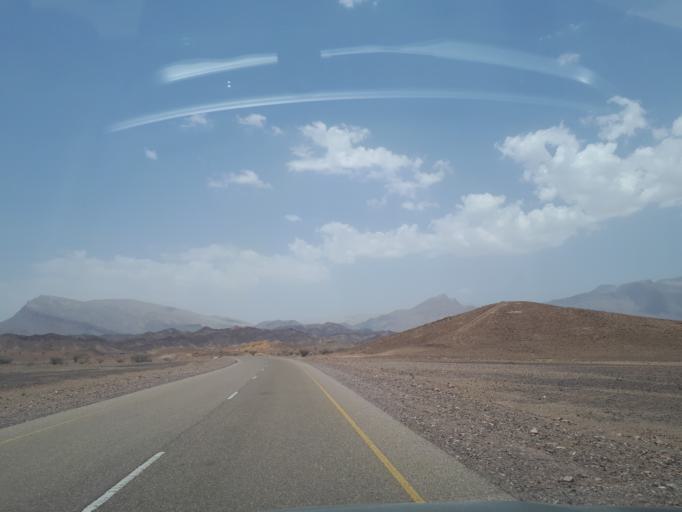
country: OM
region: Ash Sharqiyah
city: Badiyah
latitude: 22.4448
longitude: 59.0942
